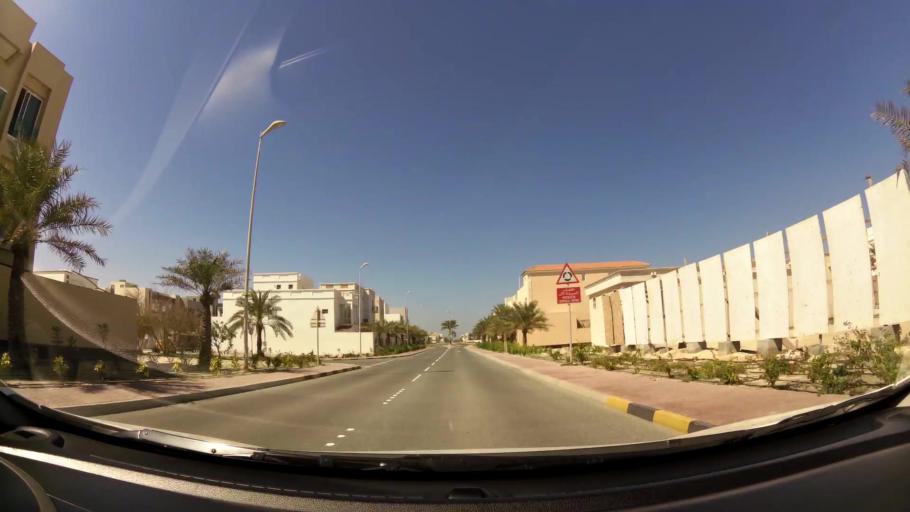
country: BH
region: Muharraq
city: Al Hadd
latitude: 26.2910
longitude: 50.6744
